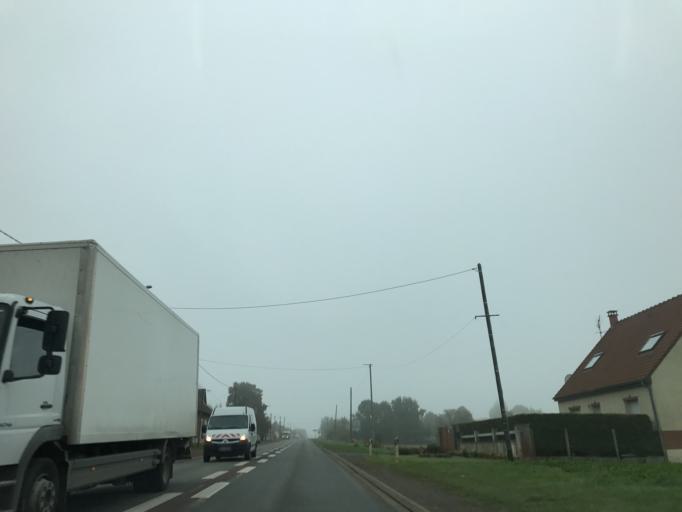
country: FR
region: Nord-Pas-de-Calais
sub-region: Departement du Pas-de-Calais
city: Bapaume
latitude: 50.0629
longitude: 2.8933
